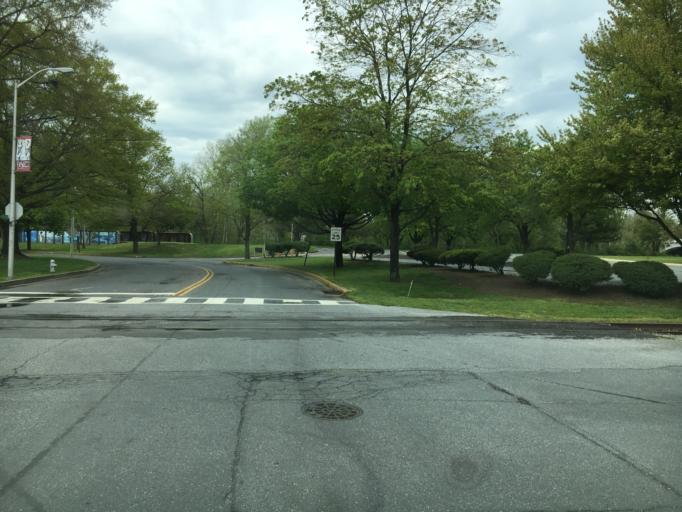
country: US
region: Pennsylvania
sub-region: Berks County
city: Reading
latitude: 40.3338
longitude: -75.9355
